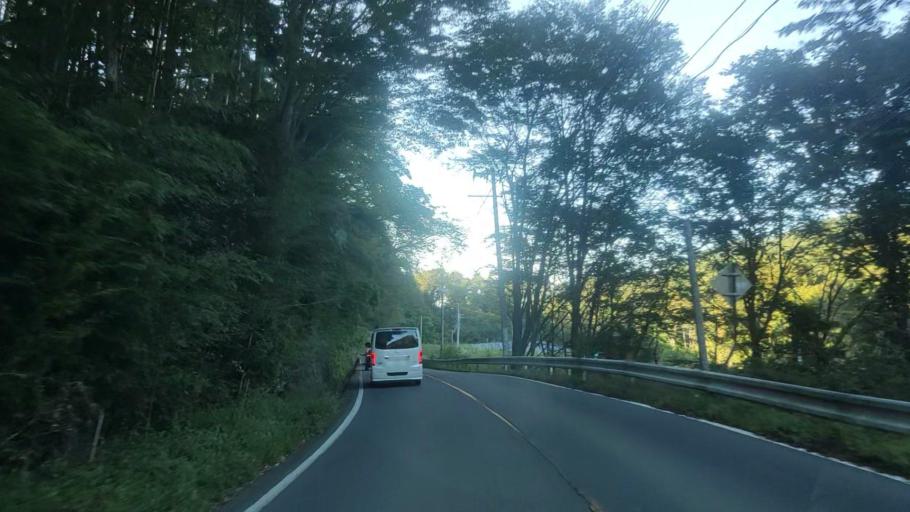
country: JP
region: Nagano
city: Kamimaruko
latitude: 36.2487
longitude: 138.3120
